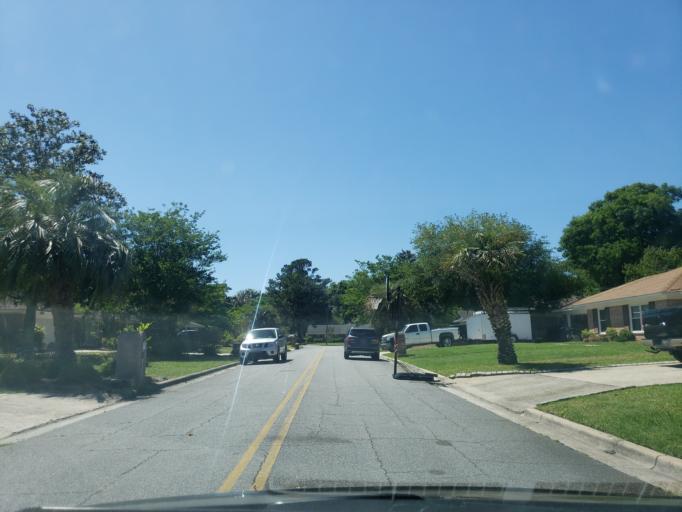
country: US
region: Georgia
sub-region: Chatham County
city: Isle of Hope
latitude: 31.9890
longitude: -81.0940
